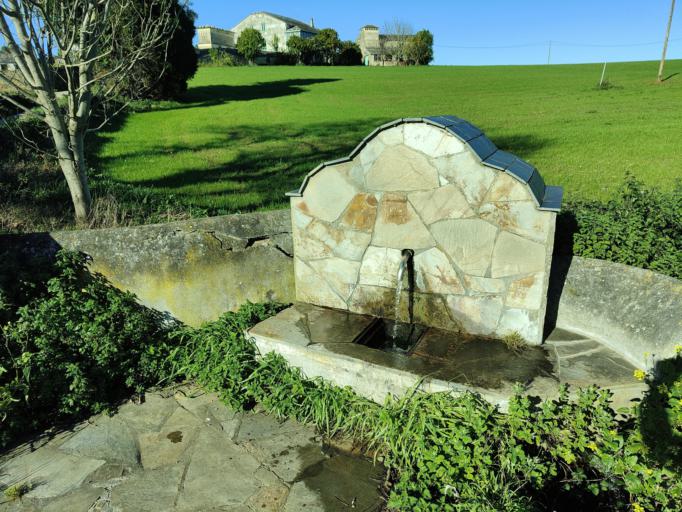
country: ES
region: Asturias
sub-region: Province of Asturias
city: Castropol
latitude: 43.5038
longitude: -7.0260
